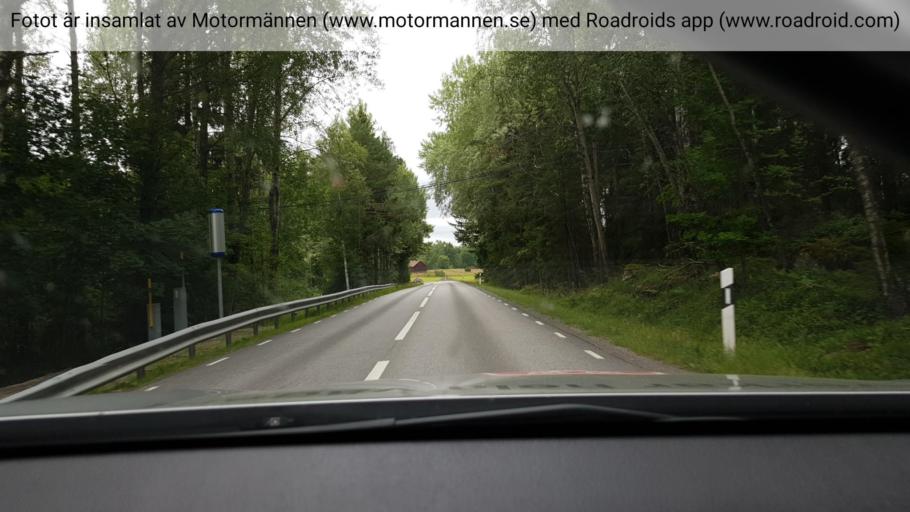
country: SE
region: Stockholm
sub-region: Norrtalje Kommun
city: Skanninge
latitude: 59.8861
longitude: 18.4893
